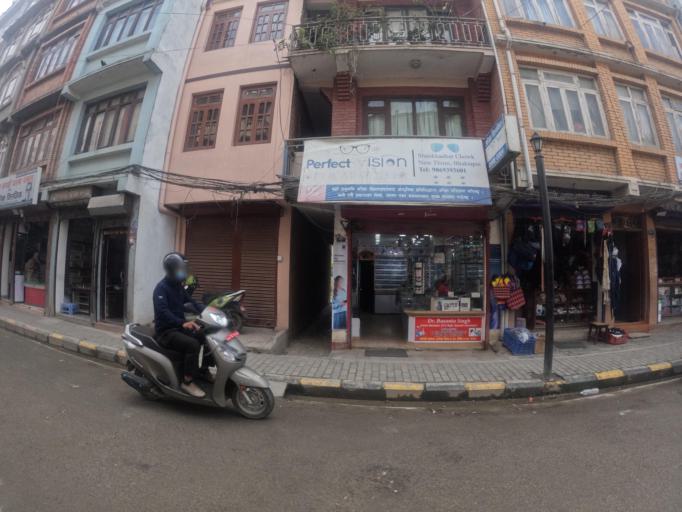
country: NP
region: Central Region
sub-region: Bagmati Zone
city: Bhaktapur
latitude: 27.6717
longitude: 85.3857
